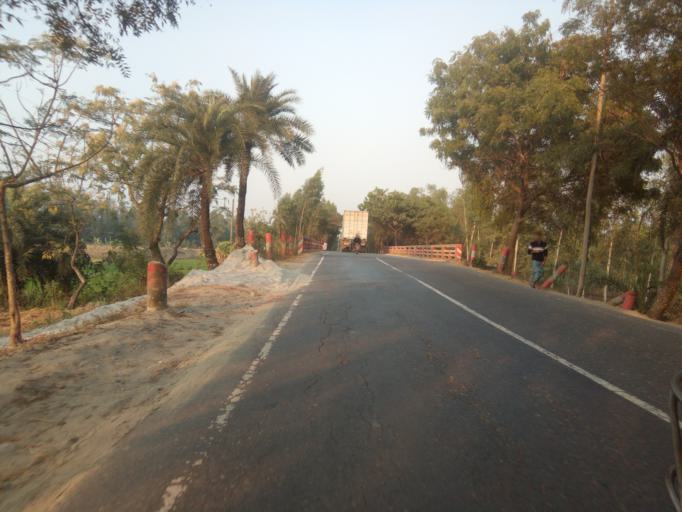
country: BD
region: Rajshahi
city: Par Naogaon
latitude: 24.5427
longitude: 89.1858
